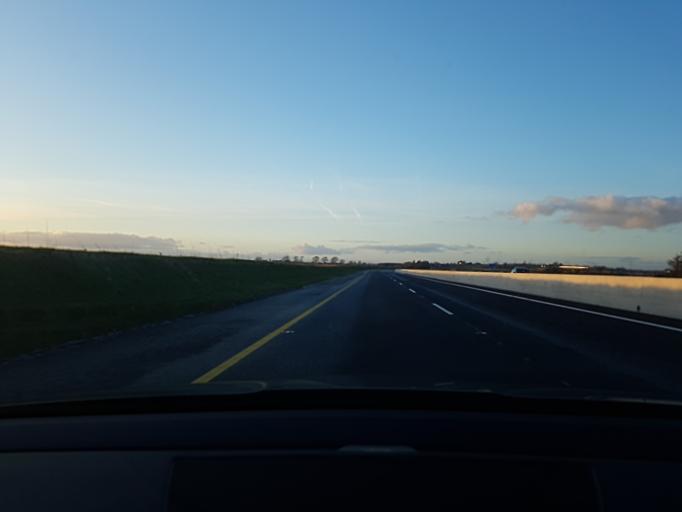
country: IE
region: Connaught
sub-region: County Galway
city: Tuam
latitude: 53.4916
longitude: -8.8710
